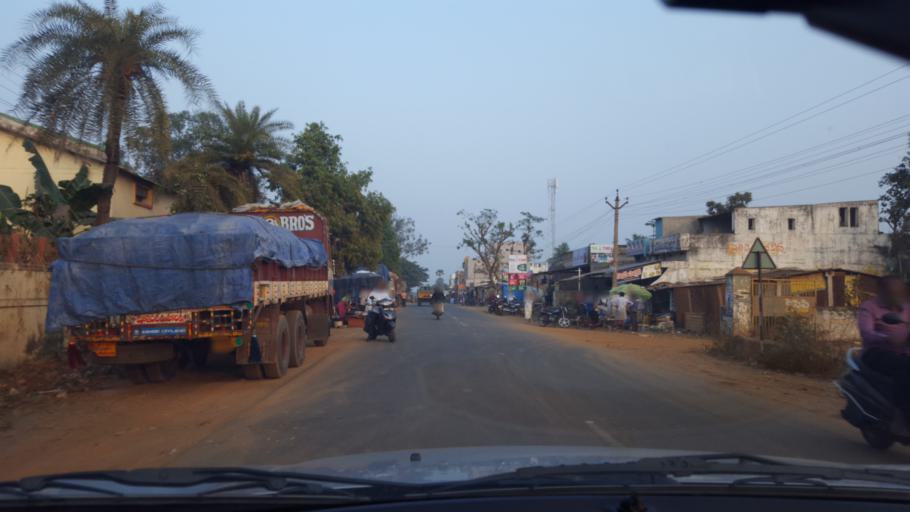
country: IN
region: Andhra Pradesh
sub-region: Srikakulam
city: Amudalavalasa
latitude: 18.3848
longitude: 83.9247
